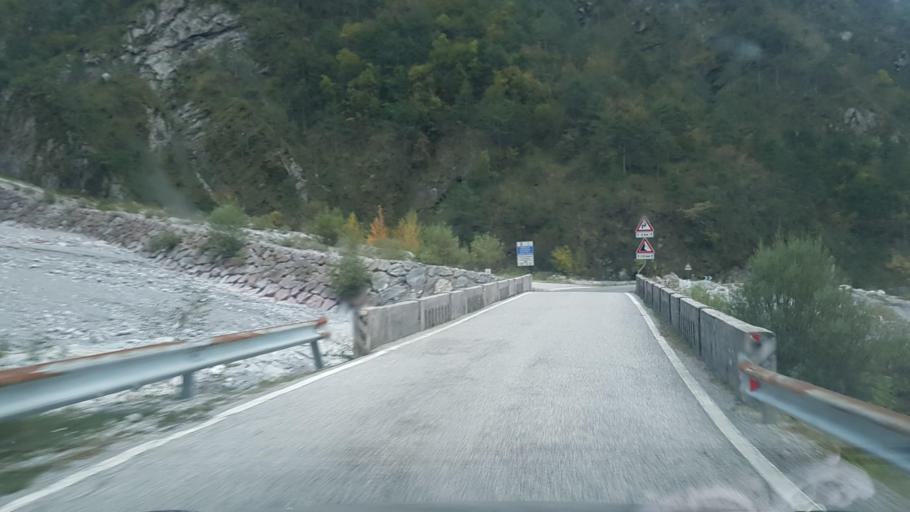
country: IT
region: Friuli Venezia Giulia
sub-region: Provincia di Udine
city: Chiaulis
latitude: 46.3344
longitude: 12.9391
